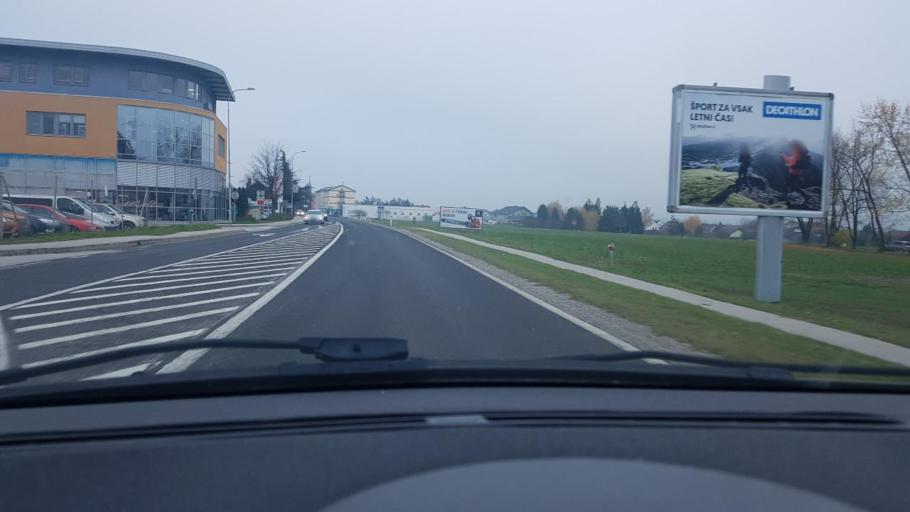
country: SI
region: Zalec
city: Sempeter v Savinj. Dolini
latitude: 46.2580
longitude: 15.1142
